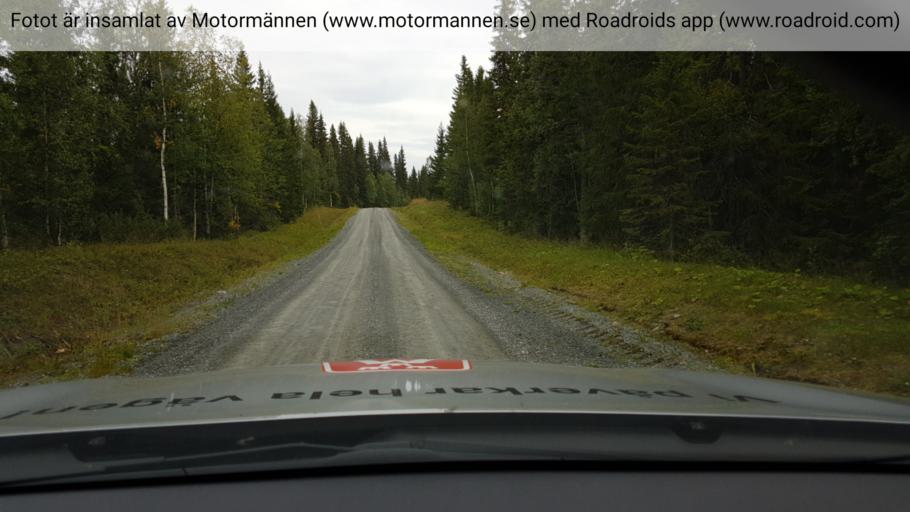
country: SE
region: Jaemtland
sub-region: Krokoms Kommun
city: Valla
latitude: 63.5813
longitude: 13.9480
